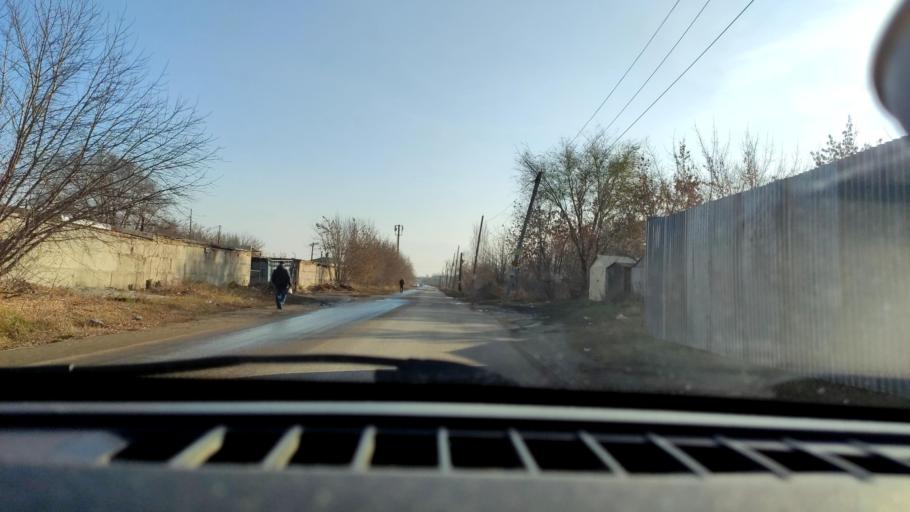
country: RU
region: Samara
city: Samara
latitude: 53.1196
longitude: 50.0978
